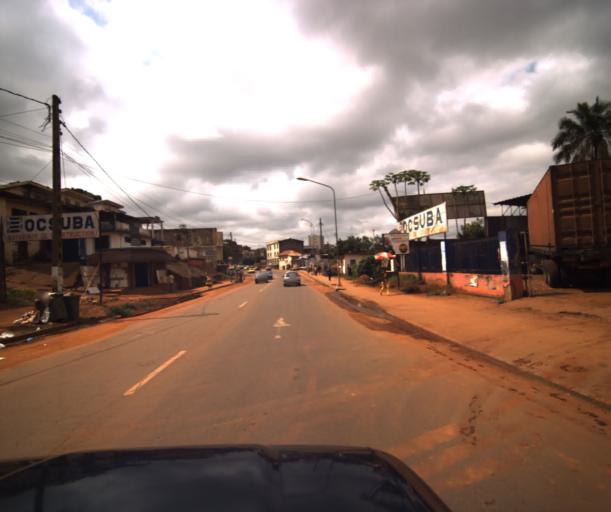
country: CM
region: Centre
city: Yaounde
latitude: 3.8552
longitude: 11.5220
